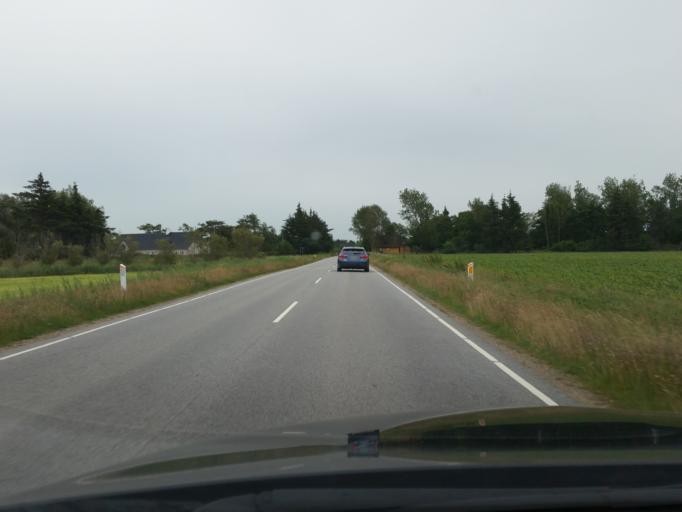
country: DK
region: South Denmark
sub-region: Varde Kommune
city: Oksbol
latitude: 55.7994
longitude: 8.2309
